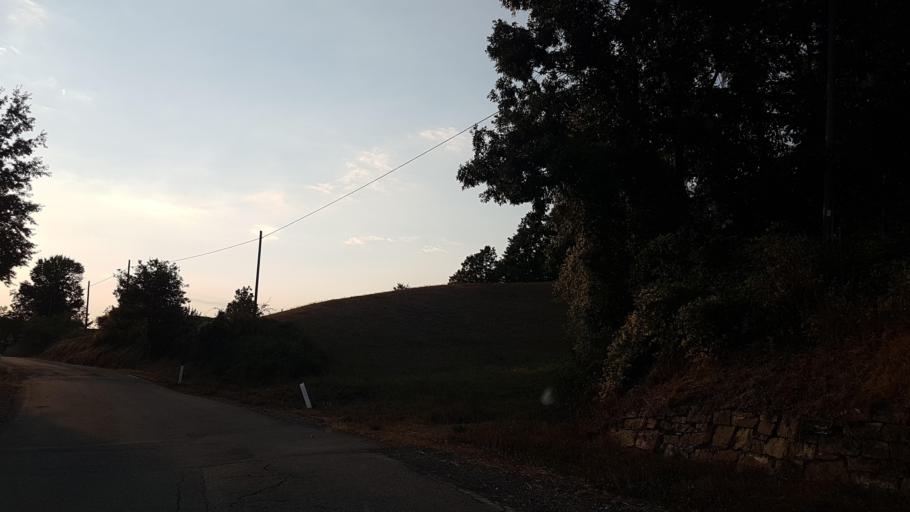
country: IT
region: Emilia-Romagna
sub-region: Provincia di Parma
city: Albareto
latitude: 44.4629
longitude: 9.6961
